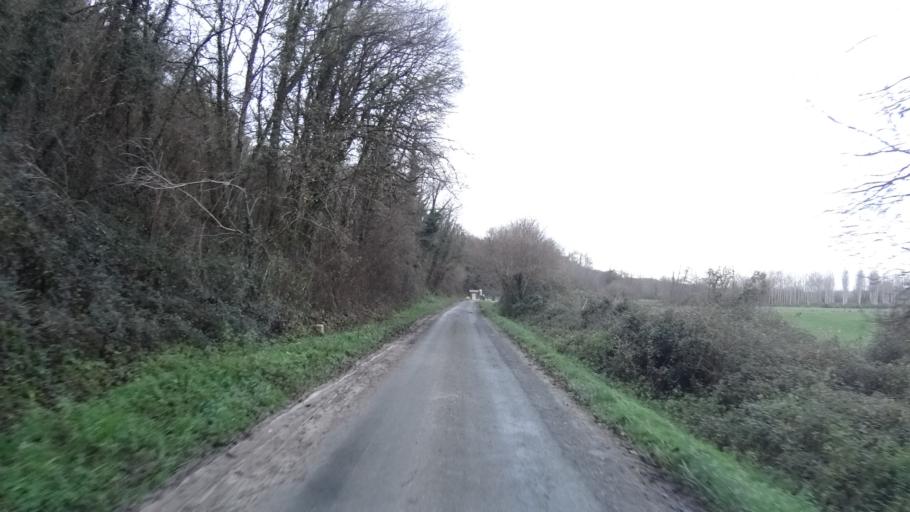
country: FR
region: Aquitaine
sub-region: Departement de la Dordogne
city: Saint-Aulaye
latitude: 45.2049
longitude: 0.1303
